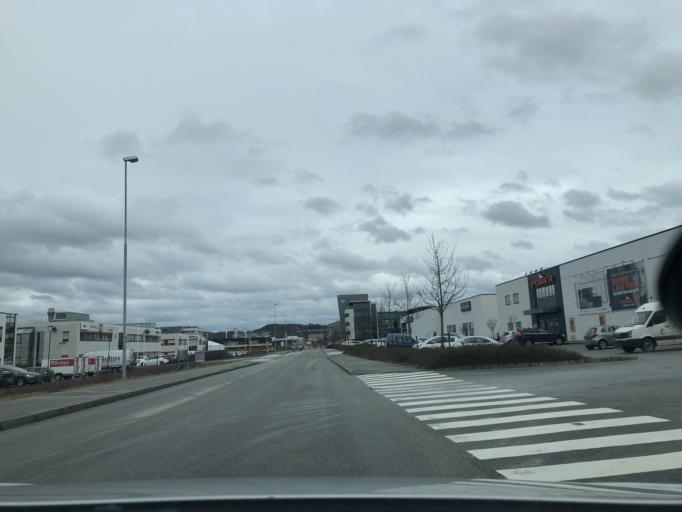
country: NO
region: Rogaland
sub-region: Sandnes
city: Sandnes
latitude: 58.8801
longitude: 5.7206
